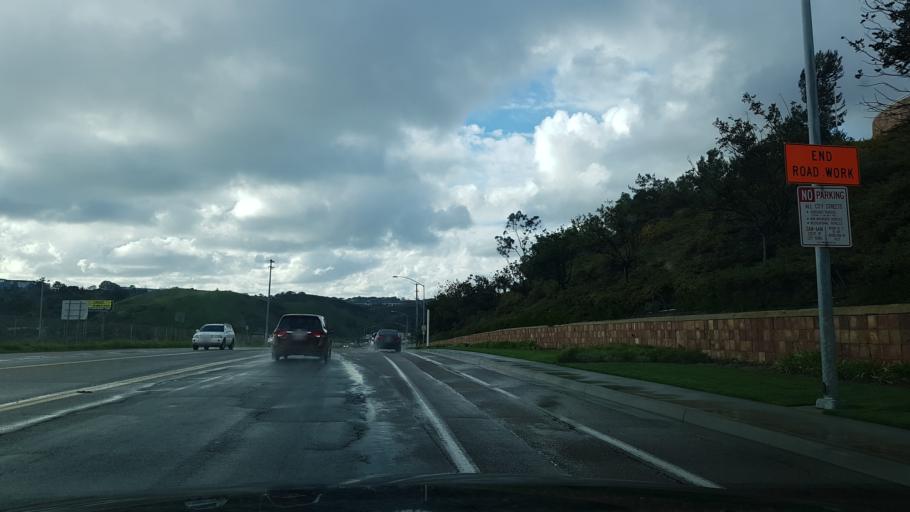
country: US
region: California
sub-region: San Diego County
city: La Jolla
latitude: 32.8927
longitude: -117.2079
